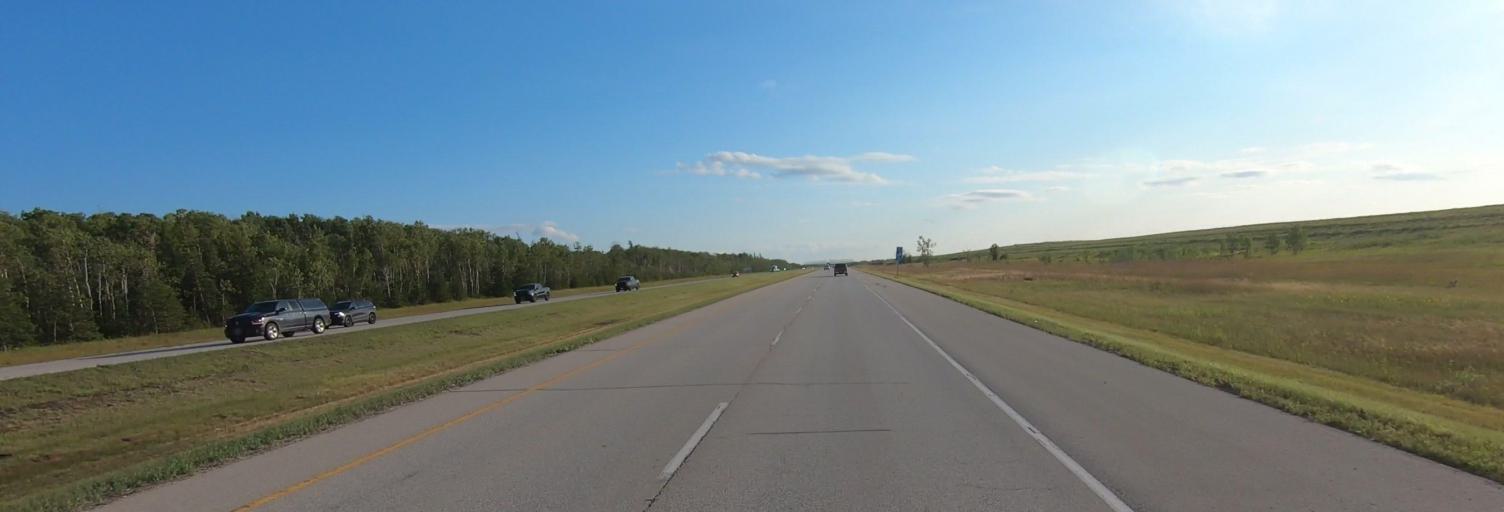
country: CA
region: Manitoba
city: Selkirk
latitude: 50.0329
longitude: -96.9254
